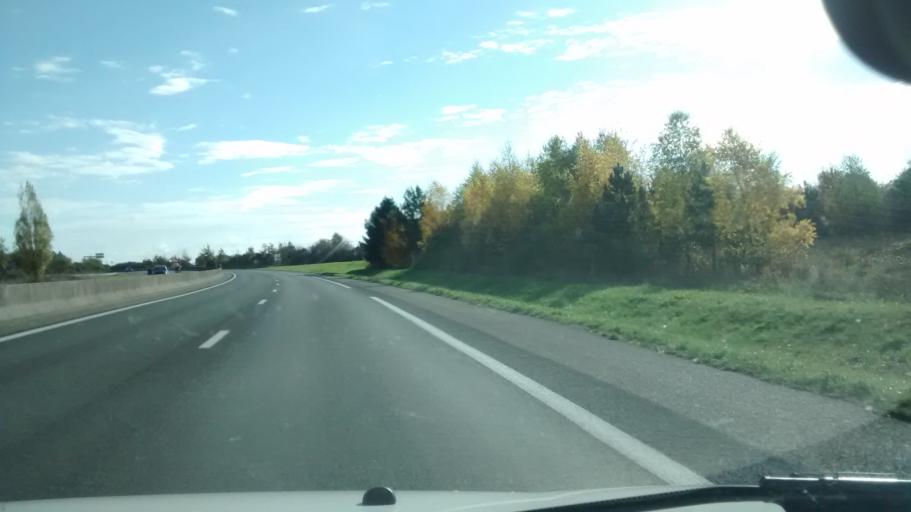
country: FR
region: Pays de la Loire
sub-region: Departement de Maine-et-Loire
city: Pouance
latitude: 47.7376
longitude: -1.1497
